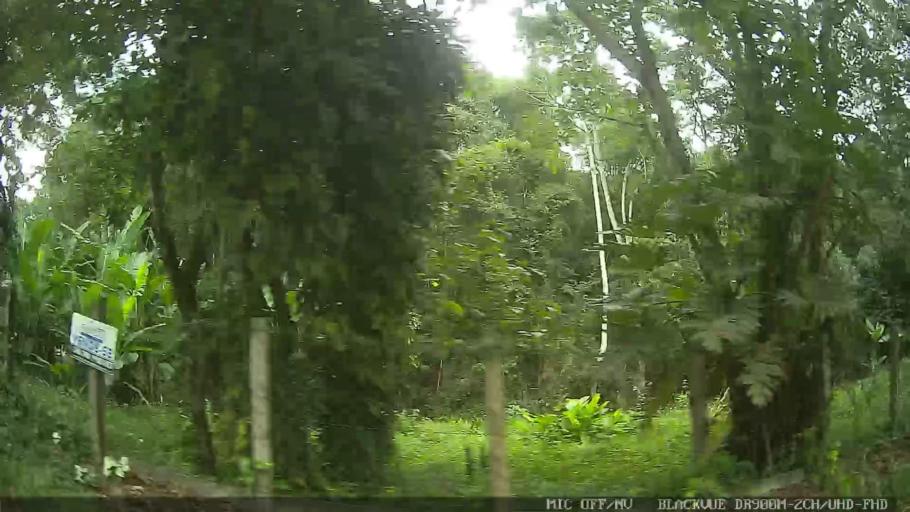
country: BR
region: Sao Paulo
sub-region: Atibaia
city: Atibaia
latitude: -23.1586
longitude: -46.5679
